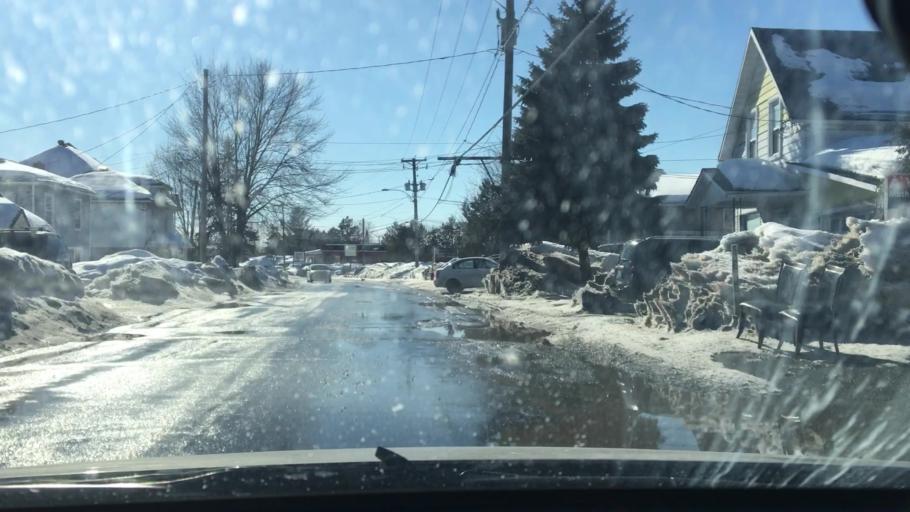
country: CA
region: Quebec
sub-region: Outaouais
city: Gatineau
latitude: 45.4698
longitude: -75.6835
